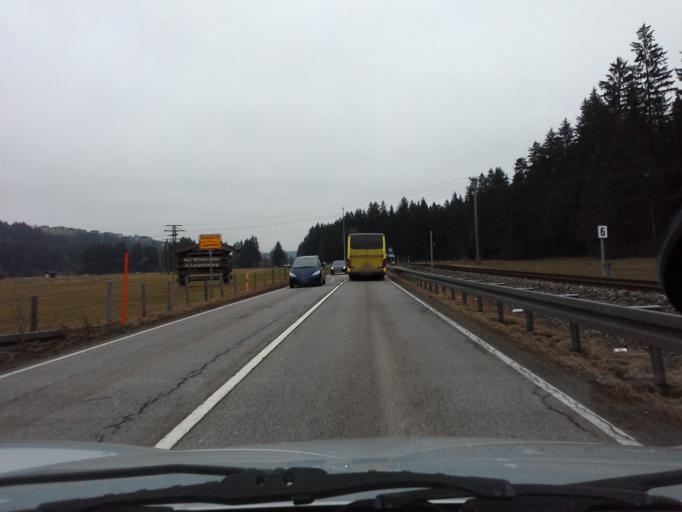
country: DE
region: Bavaria
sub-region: Swabia
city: Oberstdorf
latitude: 47.4403
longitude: 10.2755
